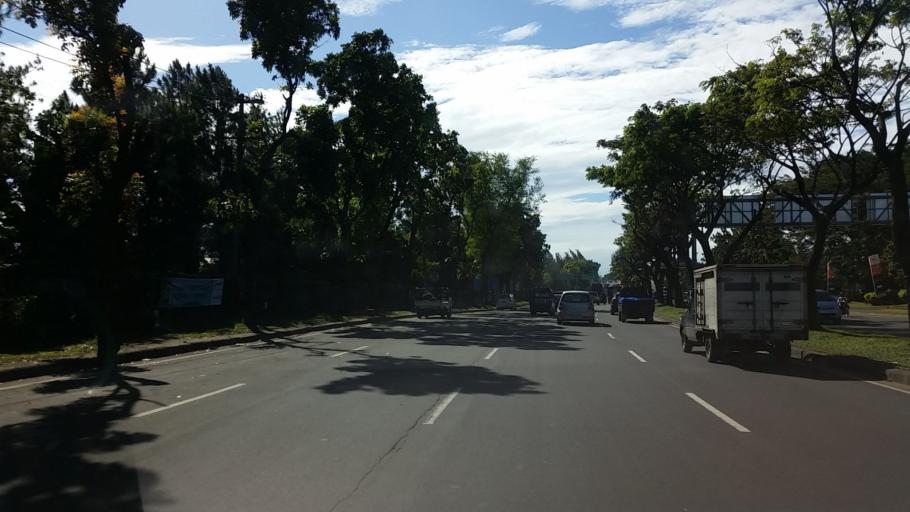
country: ID
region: West Java
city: Serpong
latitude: -6.3093
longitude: 106.6743
